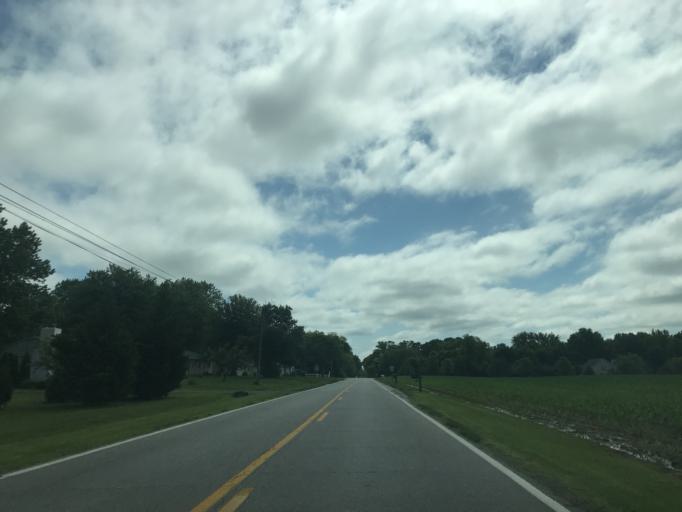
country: US
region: Maryland
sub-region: Caroline County
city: Ridgely
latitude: 38.9168
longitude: -75.9312
